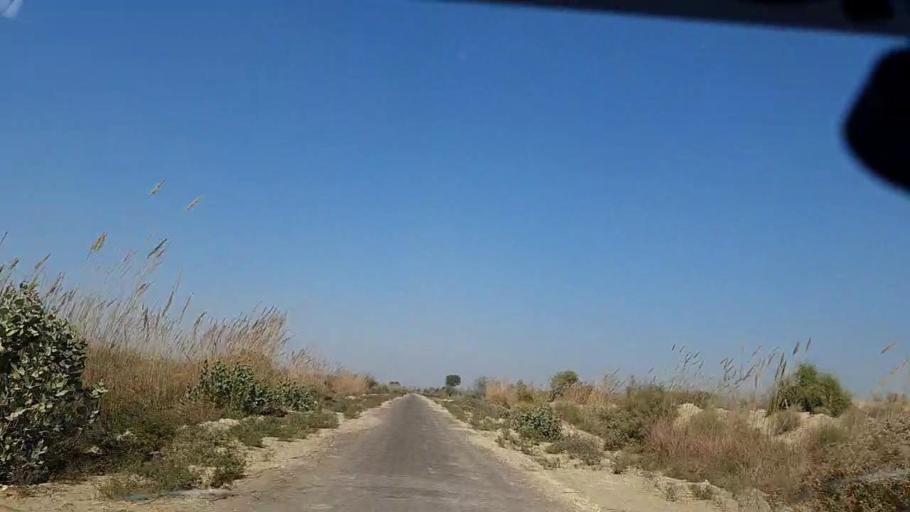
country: PK
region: Sindh
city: Khanpur
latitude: 27.5880
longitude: 69.3758
